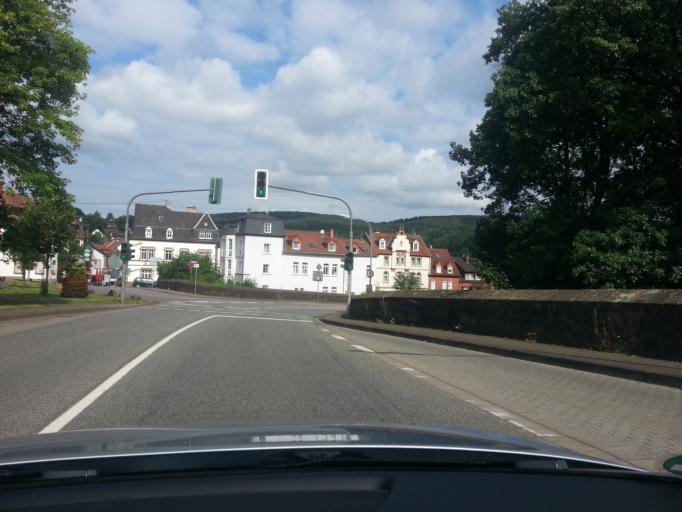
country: DE
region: Saarland
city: Mettlach
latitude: 49.4917
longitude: 6.5937
